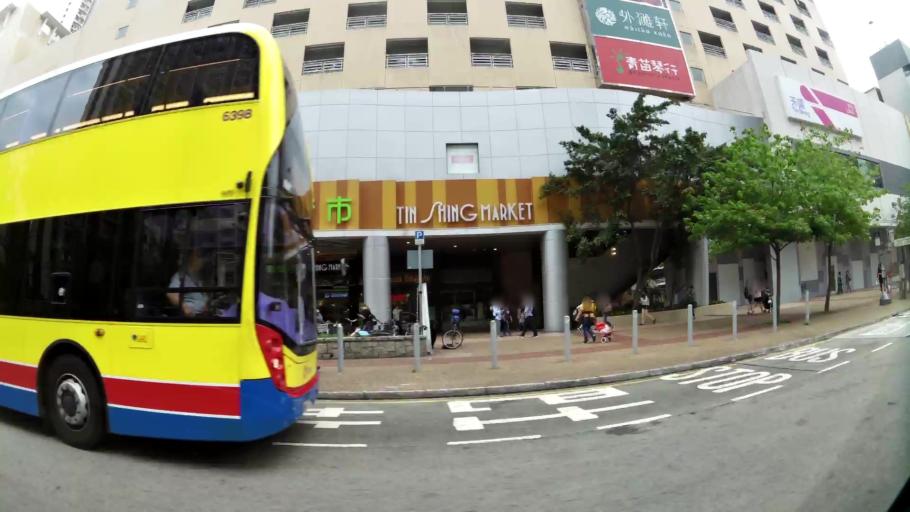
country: HK
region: Yuen Long
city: Yuen Long Kau Hui
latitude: 22.4494
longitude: 114.0030
